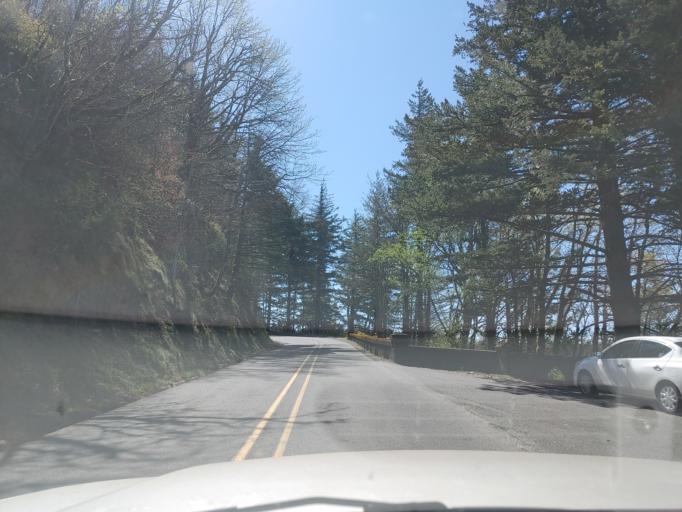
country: US
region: Washington
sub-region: Clark County
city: Washougal
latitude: 45.5379
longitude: -122.2470
